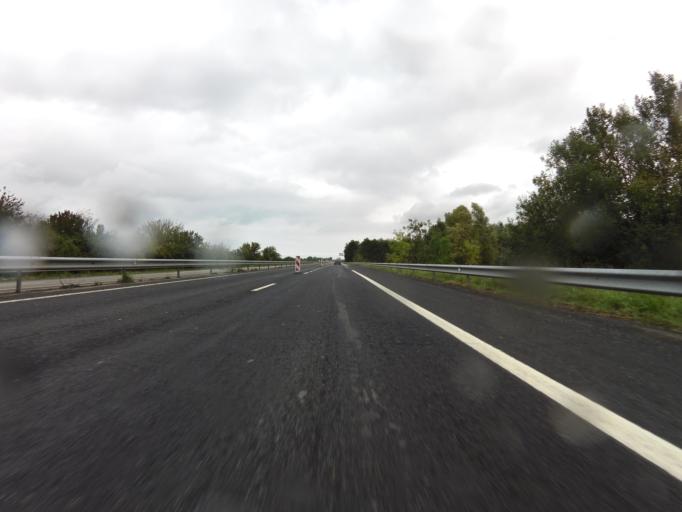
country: FR
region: Haute-Normandie
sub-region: Departement de la Seine-Maritime
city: Saint-Aubin-sur-Scie
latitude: 49.8206
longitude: 1.0639
